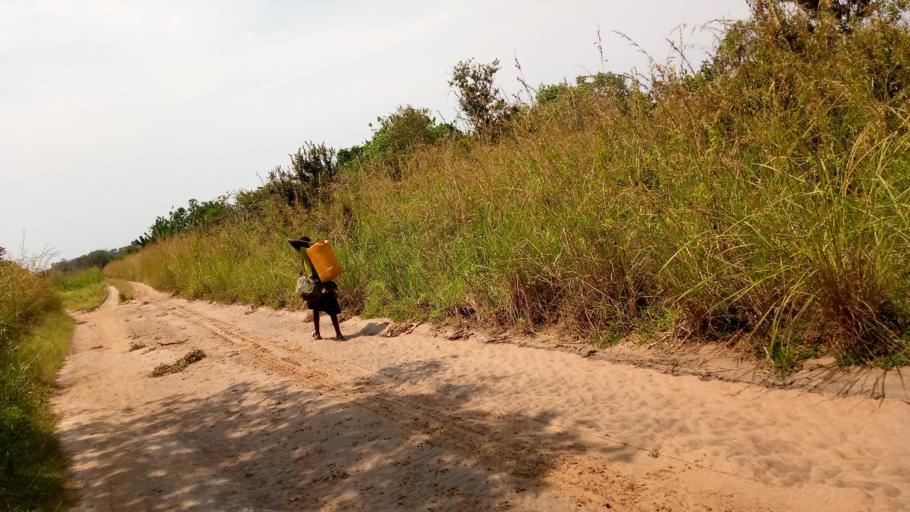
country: CD
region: Bandundu
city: Bandundu
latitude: -4.1725
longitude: 17.3951
